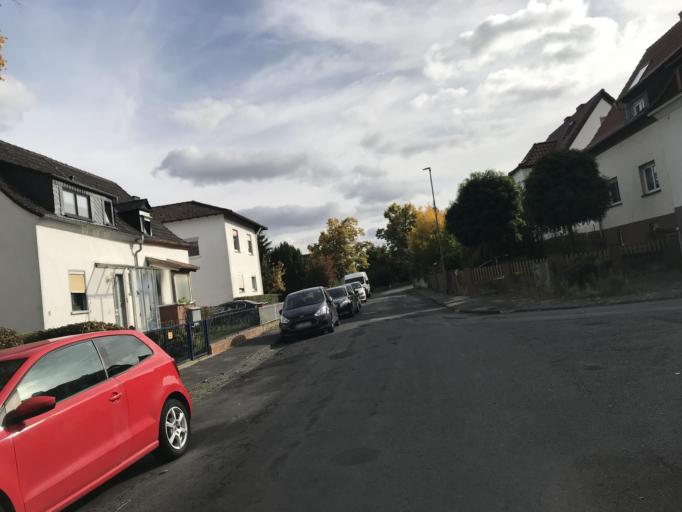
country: DE
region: Hesse
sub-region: Regierungsbezirk Darmstadt
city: Butzbach
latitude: 50.4356
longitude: 8.6565
